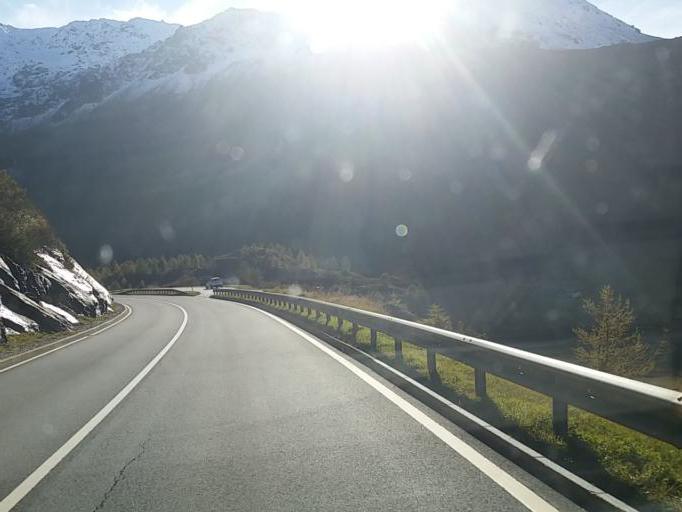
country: CH
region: Valais
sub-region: Brig District
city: Brig
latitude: 46.2337
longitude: 8.0159
